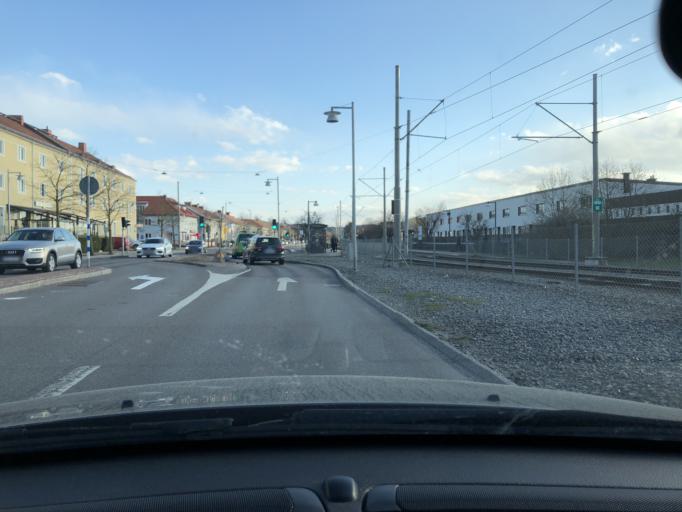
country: SE
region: Vaestra Goetaland
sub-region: Goteborg
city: Eriksbo
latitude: 57.7170
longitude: 12.0253
